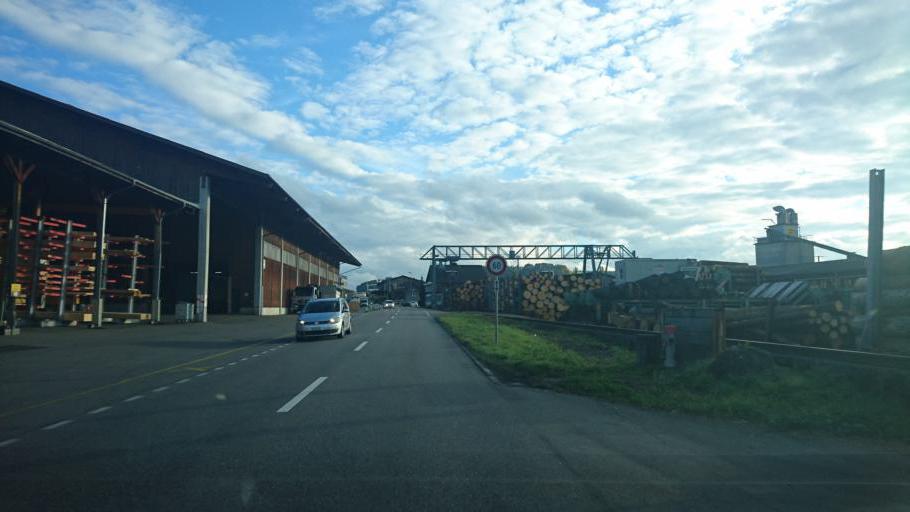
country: CH
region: Bern
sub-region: Bern-Mittelland District
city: Vechigen
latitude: 46.9412
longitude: 7.5576
